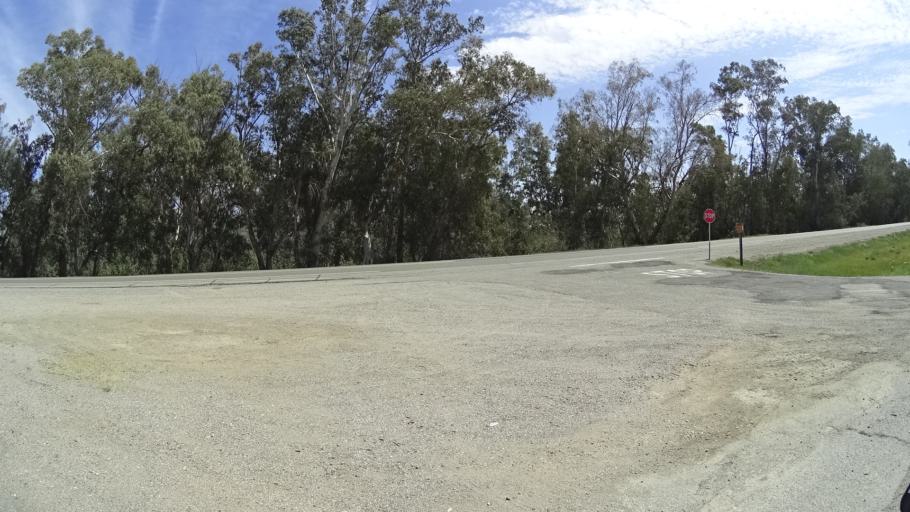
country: US
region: California
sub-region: Glenn County
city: Willows
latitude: 39.5907
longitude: -122.1951
